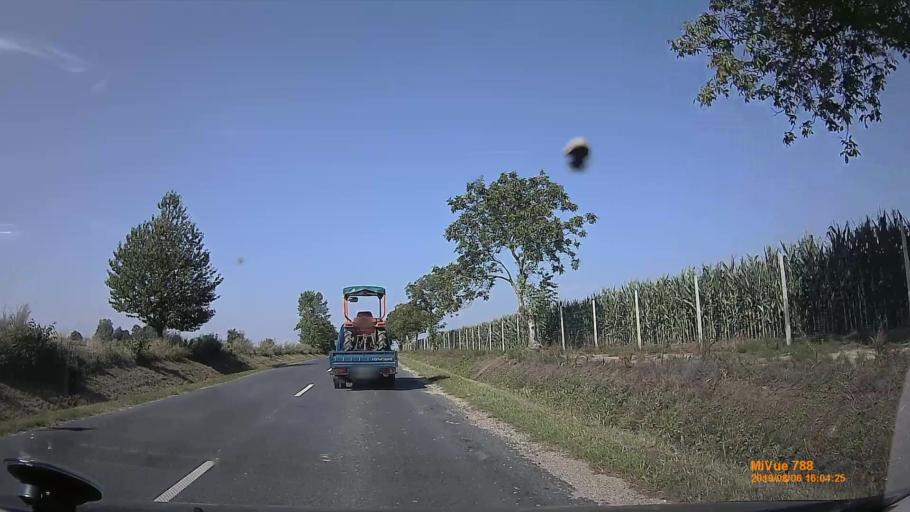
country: HU
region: Zala
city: Murakeresztur
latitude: 46.3041
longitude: 16.9582
